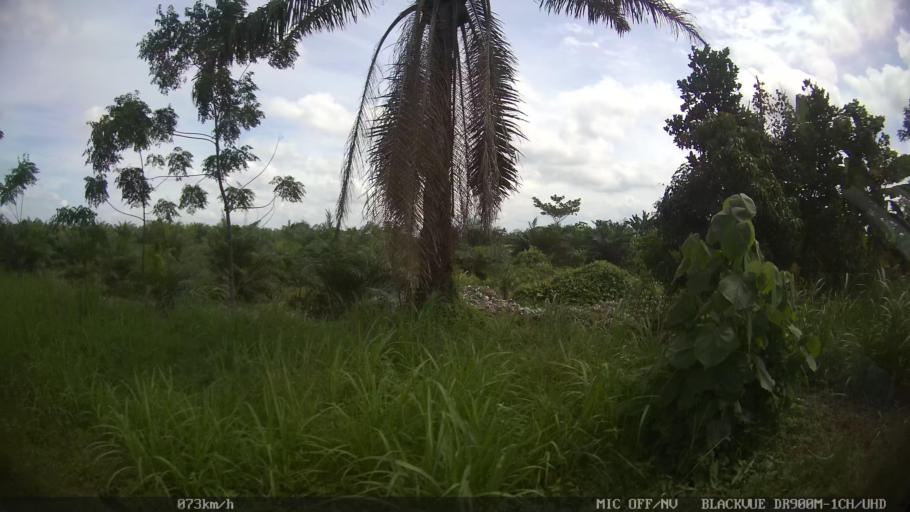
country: ID
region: North Sumatra
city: Percut
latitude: 3.5892
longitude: 98.8663
